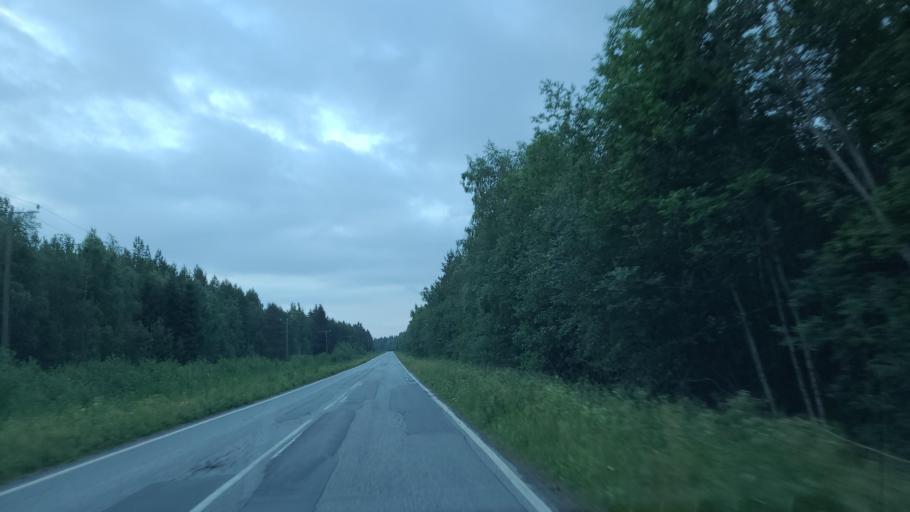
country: FI
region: Ostrobothnia
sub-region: Vaasa
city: Replot
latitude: 63.2180
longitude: 21.2478
